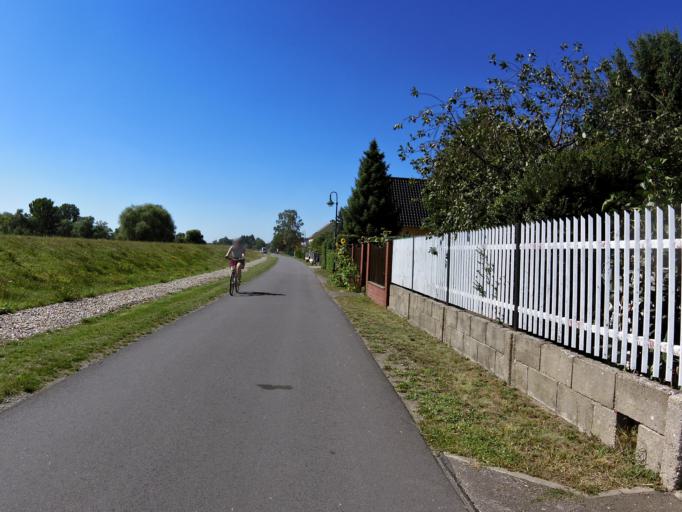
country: DE
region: Saxony-Anhalt
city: Elster
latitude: 51.8286
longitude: 12.8170
